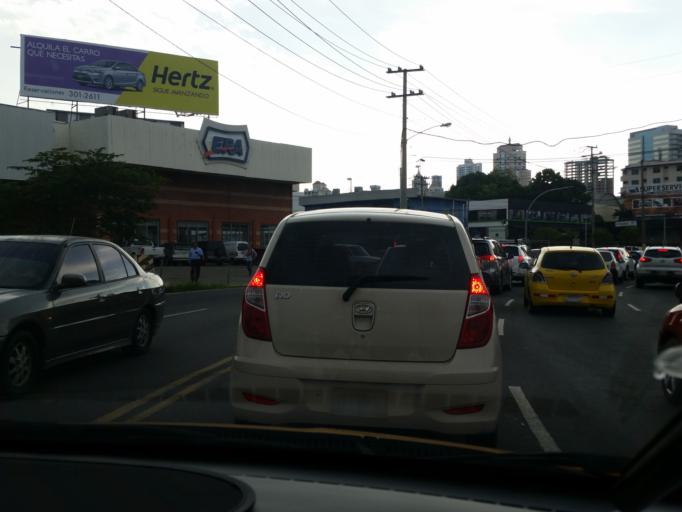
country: PA
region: Panama
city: Panama
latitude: 8.9926
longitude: -79.5180
